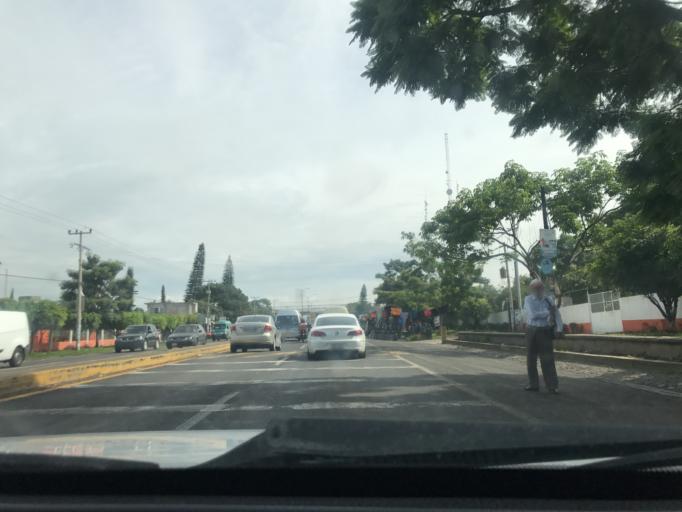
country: MX
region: Morelos
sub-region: Cuautla
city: Tierra Larga (Campo Nuevo)
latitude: 18.8709
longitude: -98.9263
